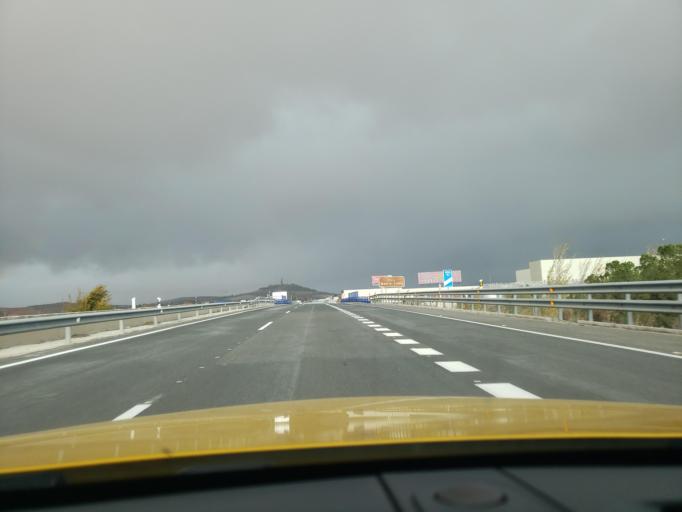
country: ES
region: Castille-La Mancha
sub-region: Provincia de Ciudad Real
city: Valdepenas
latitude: 38.7746
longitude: -3.4008
